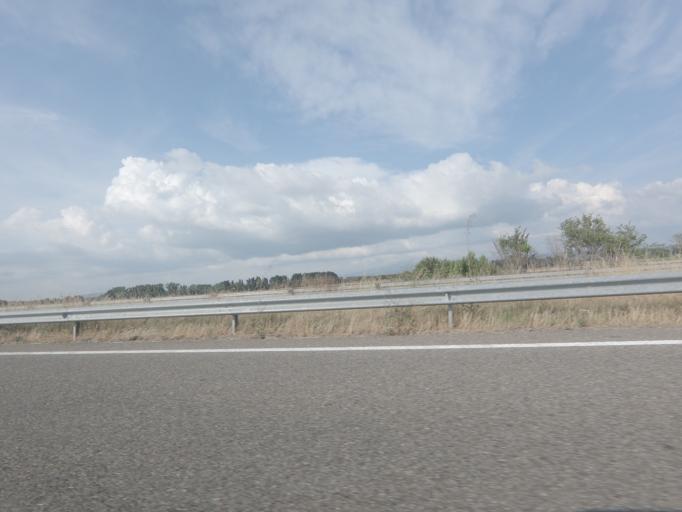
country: ES
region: Galicia
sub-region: Provincia de Ourense
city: Xinzo de Limia
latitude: 42.0962
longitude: -7.7273
